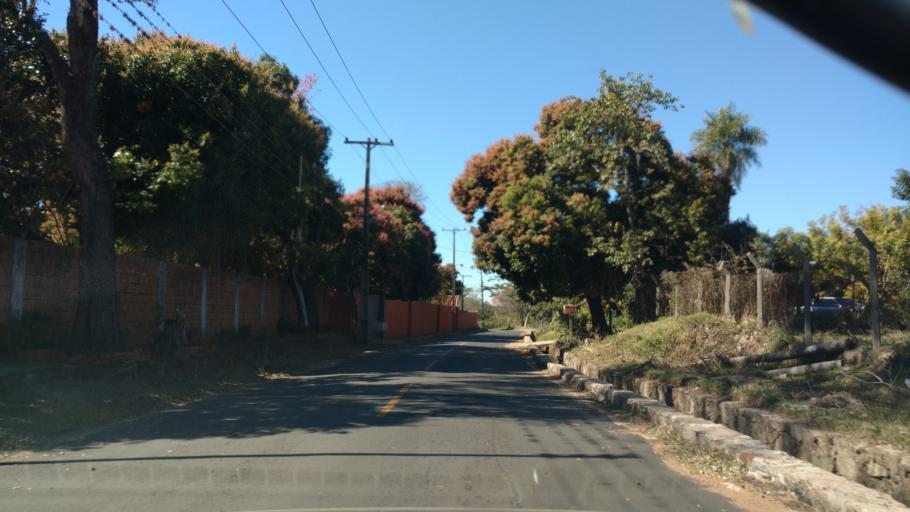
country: PY
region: Central
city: Ypacarai
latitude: -25.4150
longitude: -57.2993
